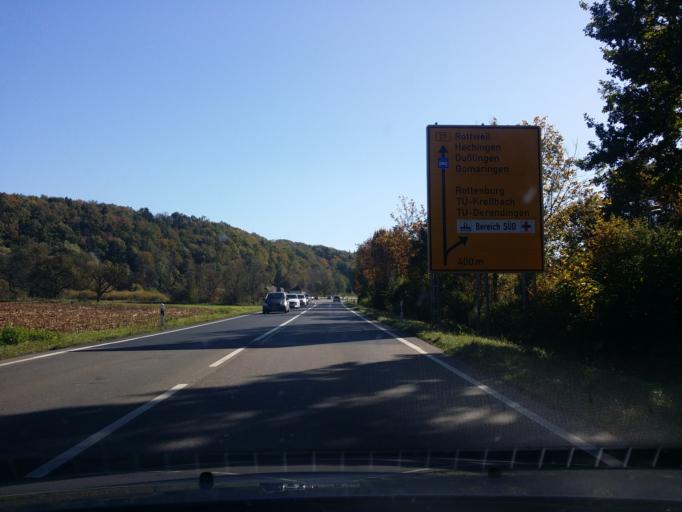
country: DE
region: Baden-Wuerttemberg
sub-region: Tuebingen Region
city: Tuebingen
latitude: 48.4920
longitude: 9.0671
